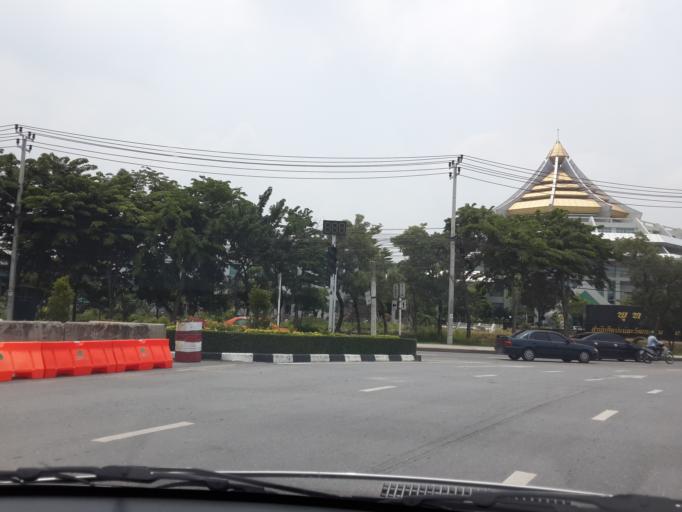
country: TH
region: Bangkok
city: Lak Si
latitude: 13.8749
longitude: 100.5963
